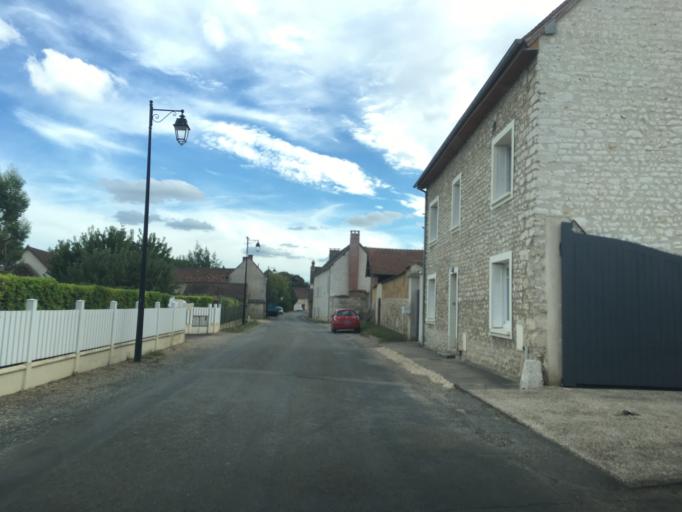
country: FR
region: Haute-Normandie
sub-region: Departement de l'Eure
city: Saint-Just
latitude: 49.1185
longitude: 1.4375
